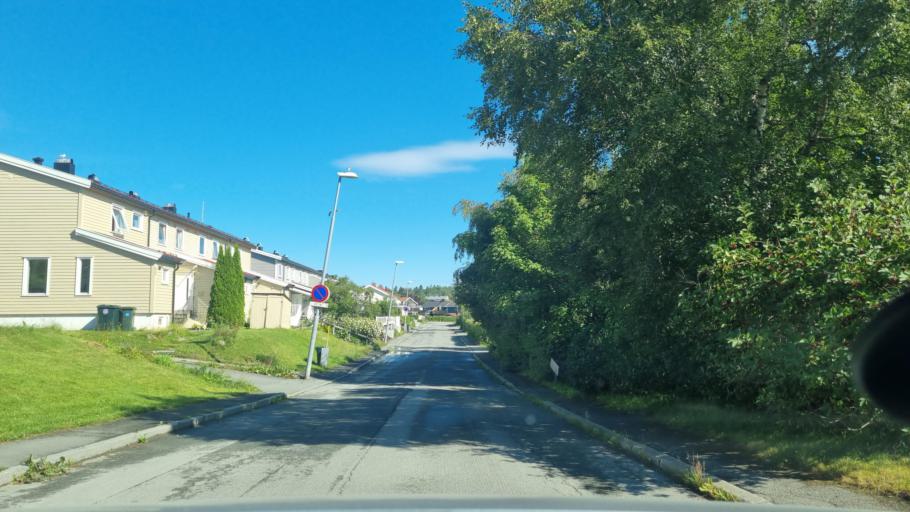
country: NO
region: Sor-Trondelag
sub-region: Trondheim
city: Trondheim
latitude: 63.4104
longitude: 10.3636
